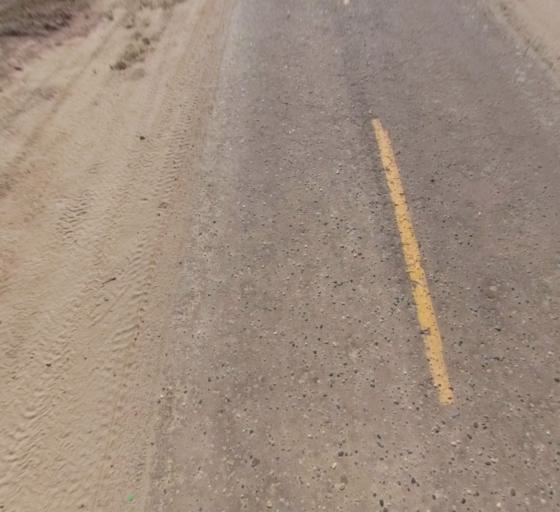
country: US
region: California
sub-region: Fresno County
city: Biola
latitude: 36.8296
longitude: -120.0212
